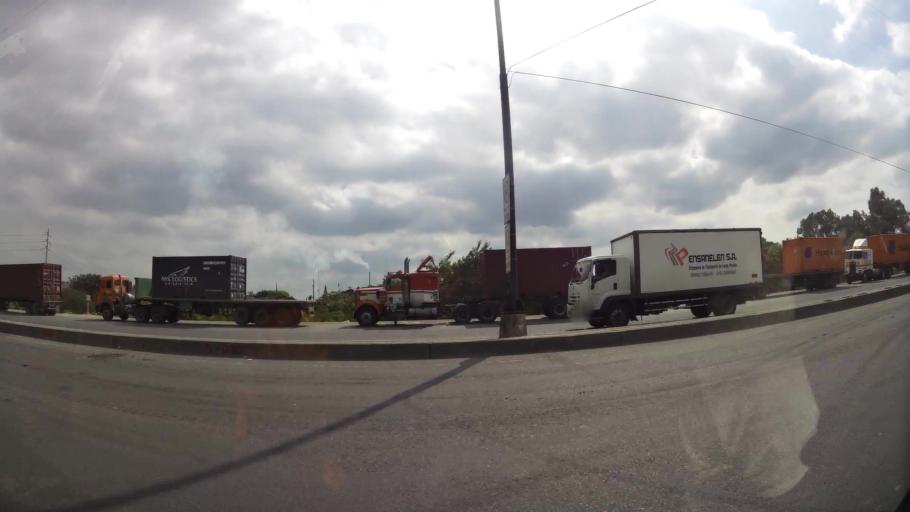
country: EC
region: Guayas
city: Santa Lucia
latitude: -2.0887
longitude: -79.9475
